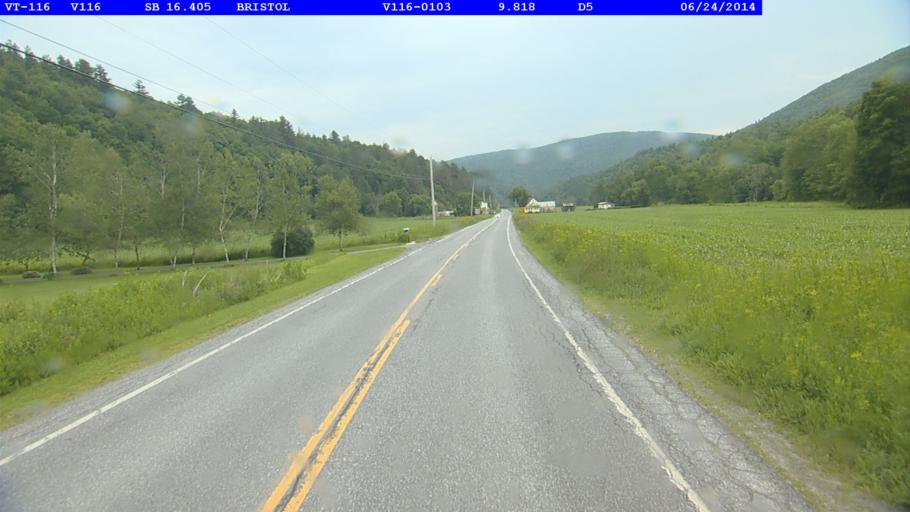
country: US
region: Vermont
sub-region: Addison County
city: Bristol
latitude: 44.1521
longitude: -73.0453
